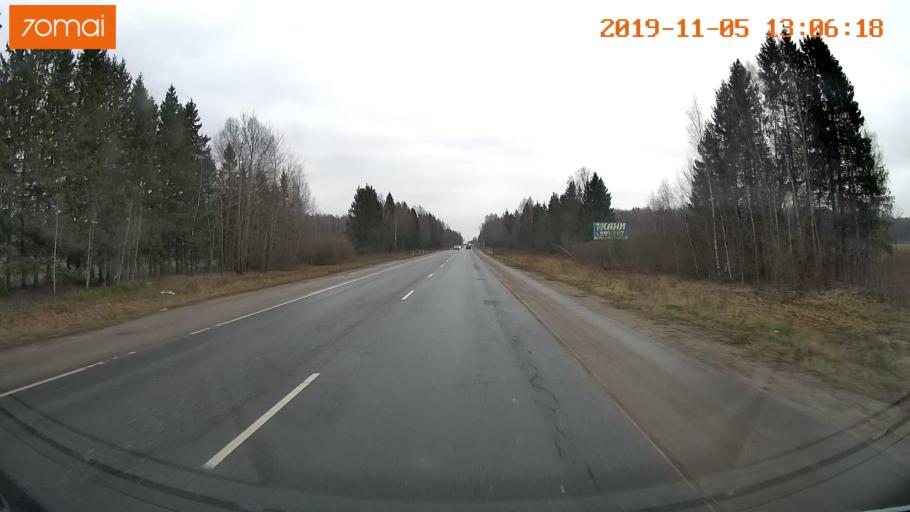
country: RU
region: Ivanovo
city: Kitovo
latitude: 56.8765
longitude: 41.2609
